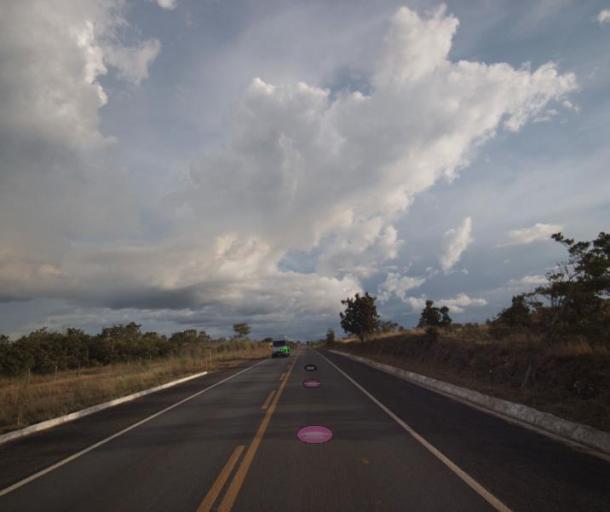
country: BR
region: Goias
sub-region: Barro Alto
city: Barro Alto
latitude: -14.8105
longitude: -48.6358
